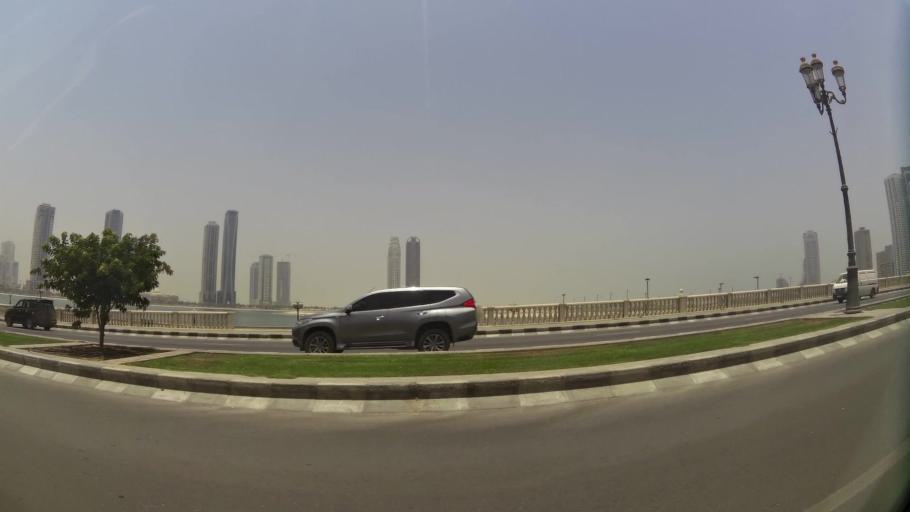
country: AE
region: Ash Shariqah
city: Sharjah
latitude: 25.3208
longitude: 55.3744
